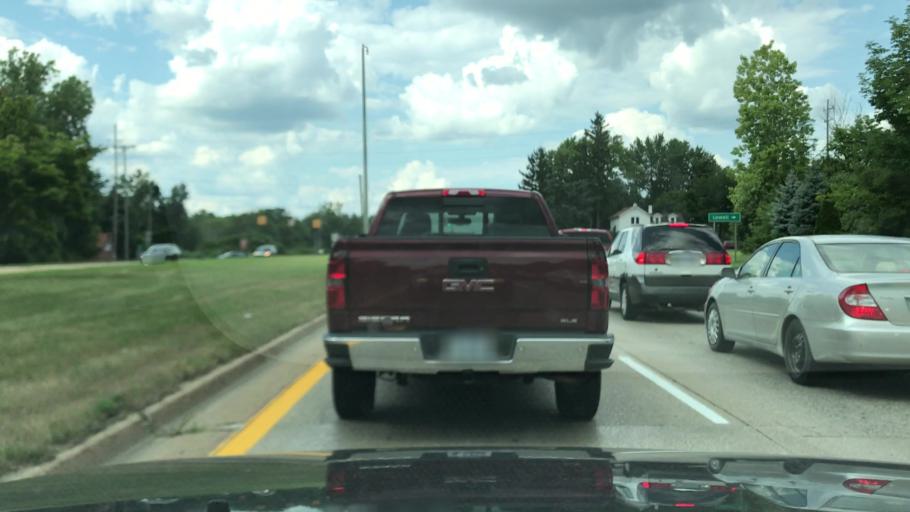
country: US
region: Michigan
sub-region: Kent County
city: East Grand Rapids
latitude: 42.9616
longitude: -85.5900
